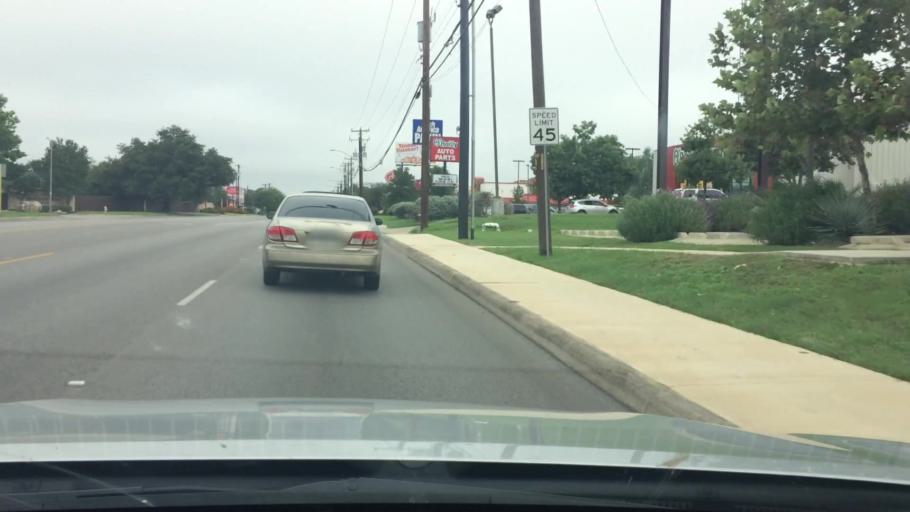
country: US
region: Texas
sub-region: Bexar County
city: Hollywood Park
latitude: 29.5730
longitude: -98.4367
